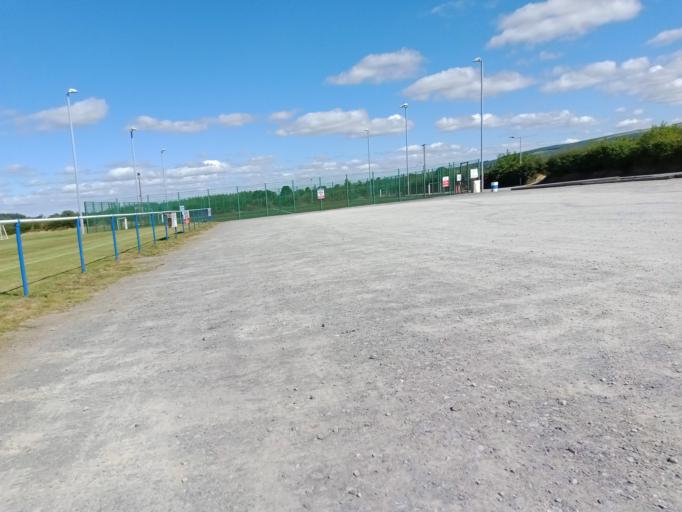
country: IE
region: Leinster
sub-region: Kilkenny
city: Thomastown
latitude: 52.5399
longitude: -7.1398
